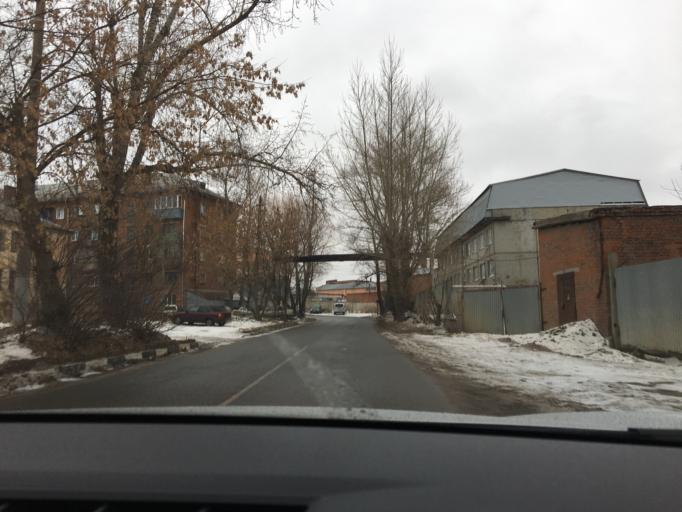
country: RU
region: Tula
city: Mendeleyevskiy
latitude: 54.1619
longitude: 37.5733
